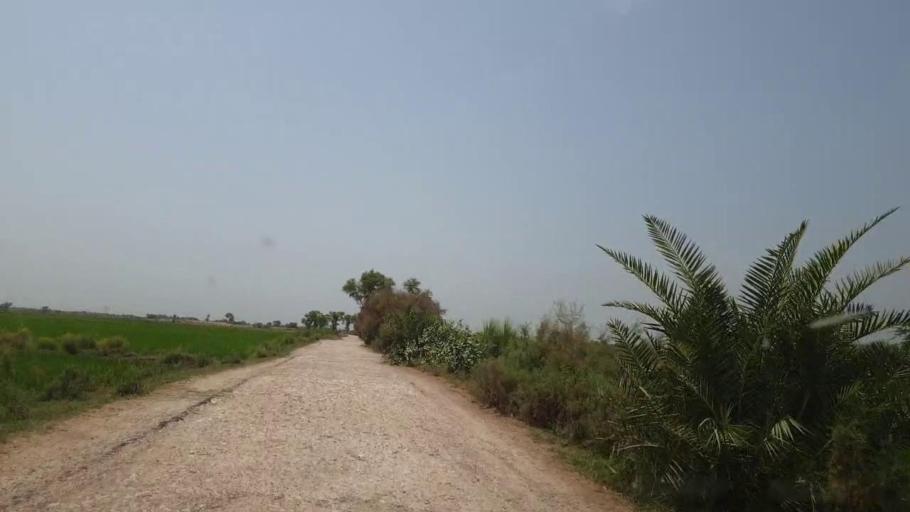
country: PK
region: Sindh
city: Shikarpur
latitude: 27.9092
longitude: 68.6339
